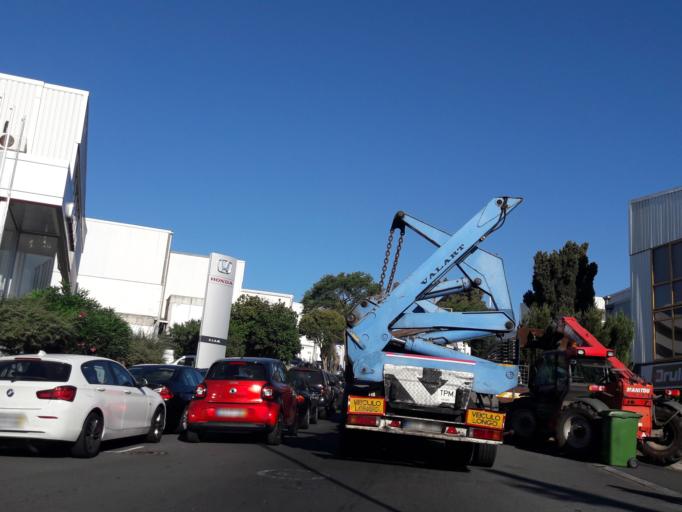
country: PT
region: Madeira
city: Canico
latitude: 32.6499
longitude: -16.8578
